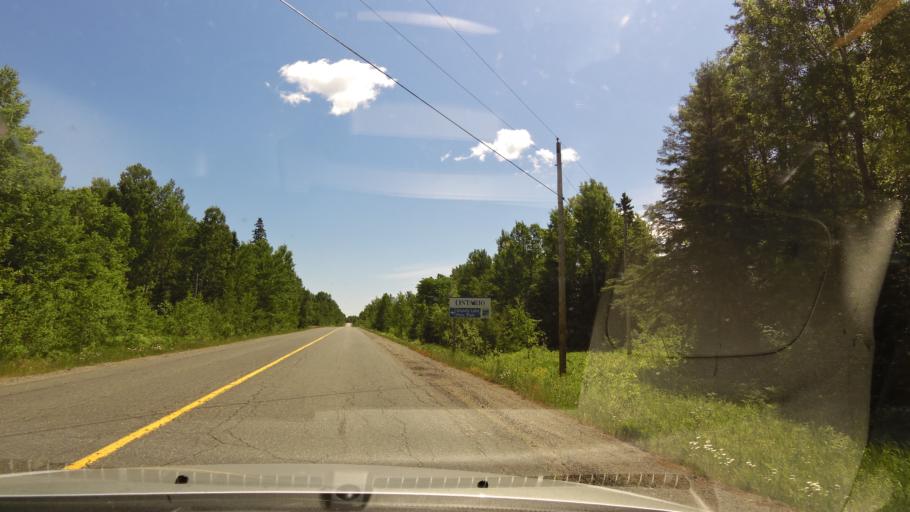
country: CA
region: Ontario
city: Greater Sudbury
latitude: 45.9130
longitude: -80.5629
